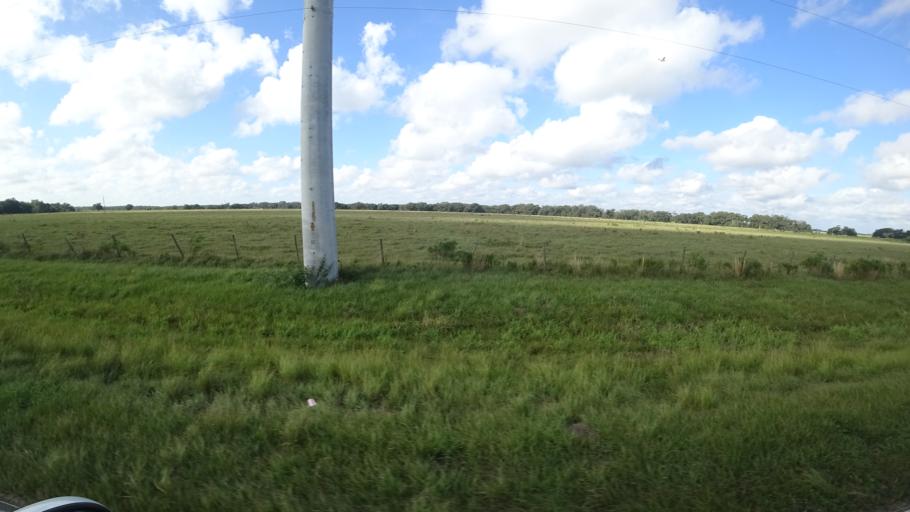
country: US
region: Florida
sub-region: Hillsborough County
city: Wimauma
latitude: 27.5048
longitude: -82.3171
